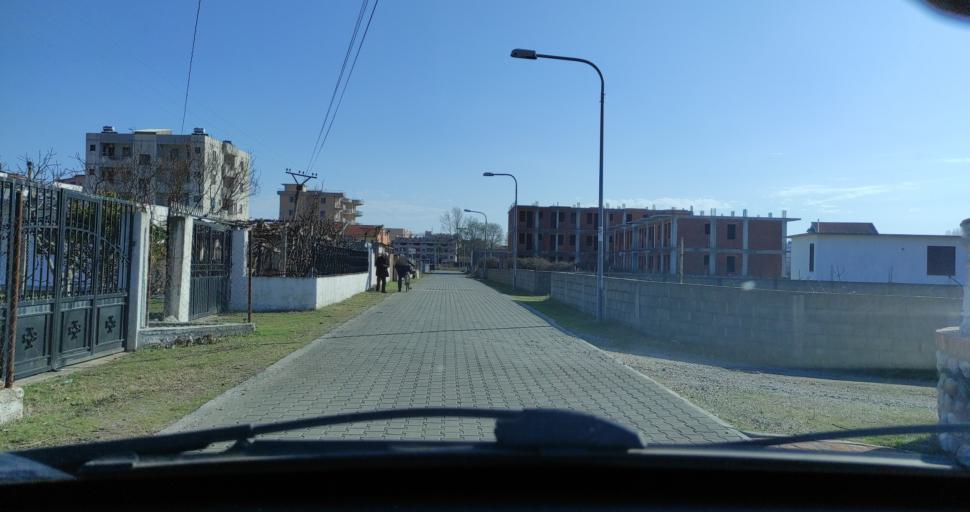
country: AL
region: Shkoder
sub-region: Rrethi i Shkodres
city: Velipoje
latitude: 41.8679
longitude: 19.4212
